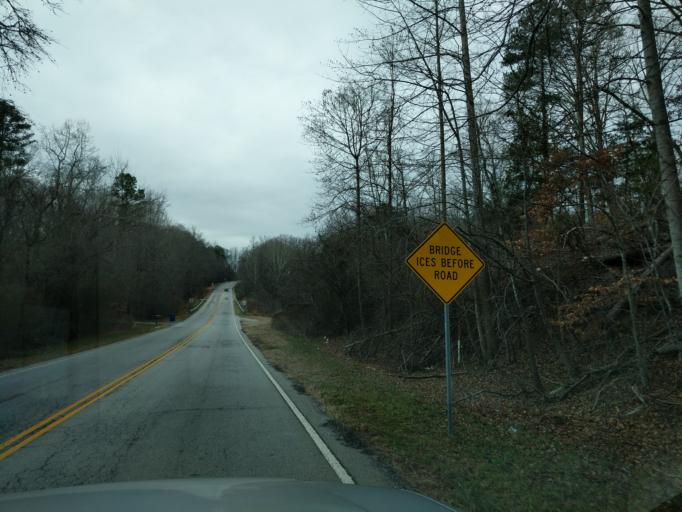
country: US
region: South Carolina
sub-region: Spartanburg County
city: Wellford
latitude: 34.8746
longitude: -82.0801
